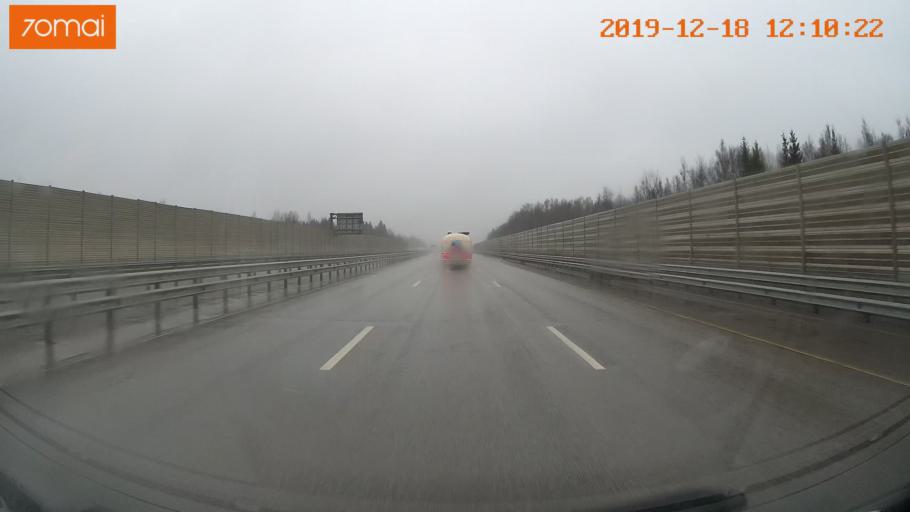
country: RU
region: Moskovskaya
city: Rumyantsevo
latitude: 55.9179
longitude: 36.5933
